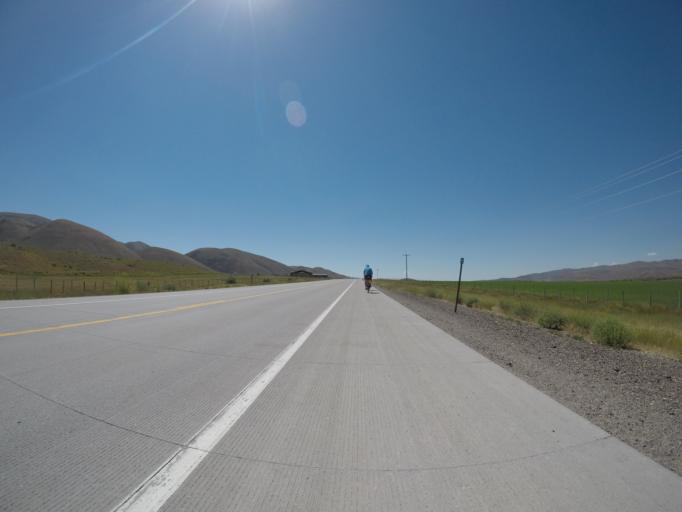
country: US
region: Idaho
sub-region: Bear Lake County
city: Montpelier
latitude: 42.1606
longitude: -110.9862
